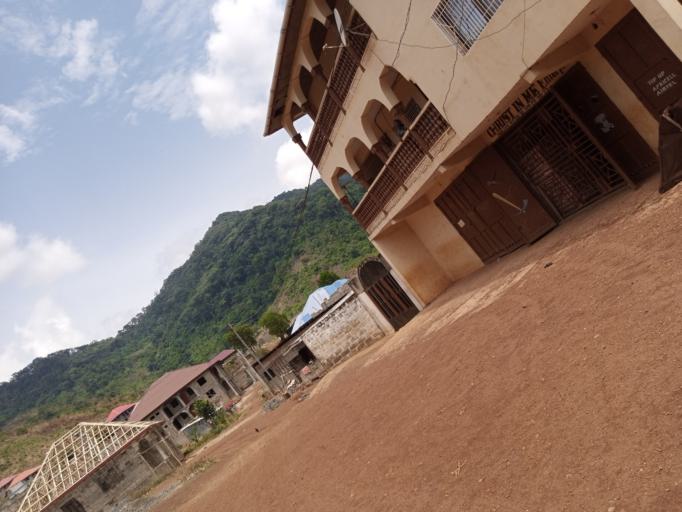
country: SL
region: Western Area
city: Hastings
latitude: 8.3721
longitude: -13.1456
